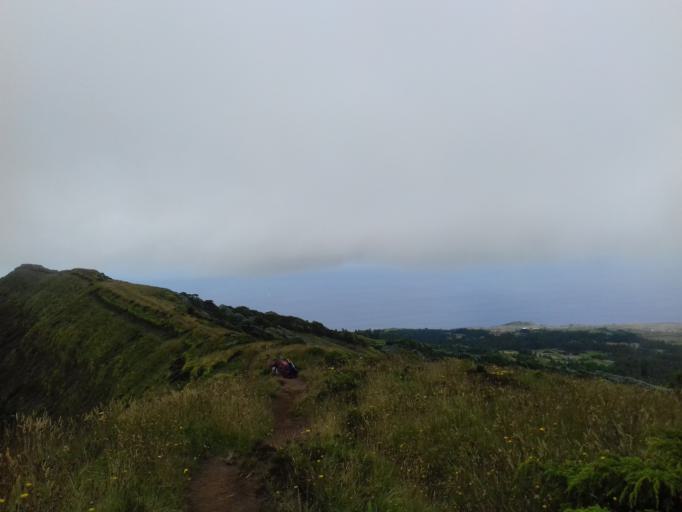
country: PT
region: Azores
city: Ribeira Grande
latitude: 38.5910
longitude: -28.7061
